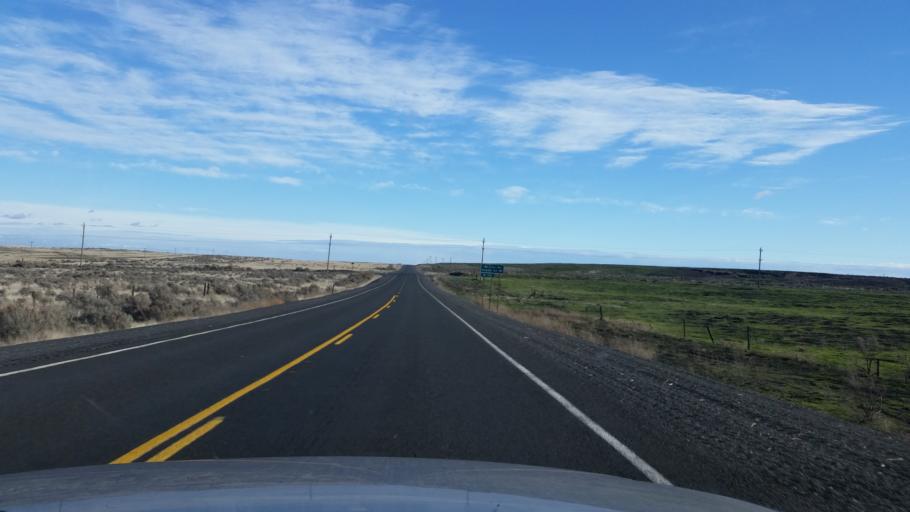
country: US
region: Washington
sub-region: Grant County
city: Warden
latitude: 47.3182
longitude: -118.8509
